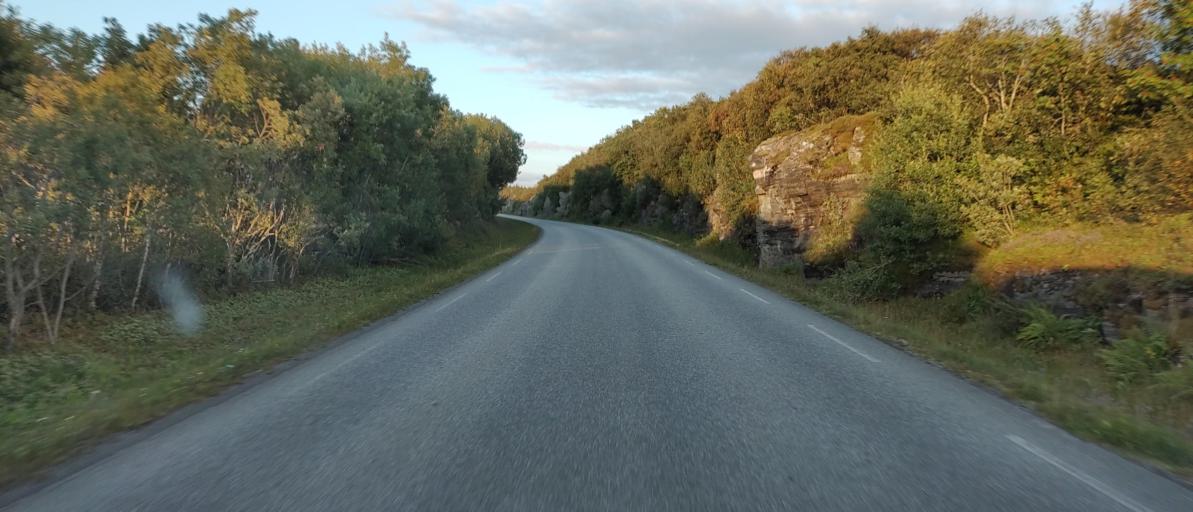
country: NO
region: More og Romsdal
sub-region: Fraena
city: Elnesvagen
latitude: 62.9909
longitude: 7.1840
